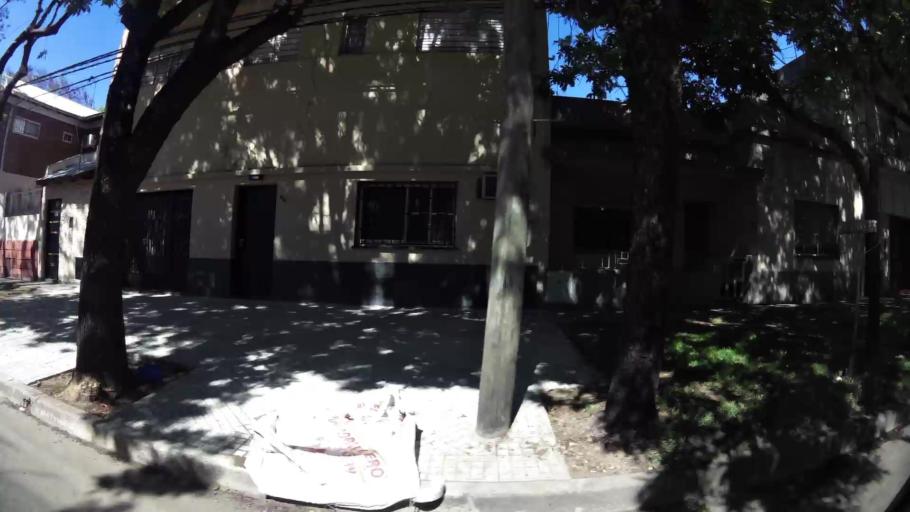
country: AR
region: Santa Fe
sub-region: Departamento de Rosario
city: Rosario
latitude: -32.9389
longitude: -60.6947
